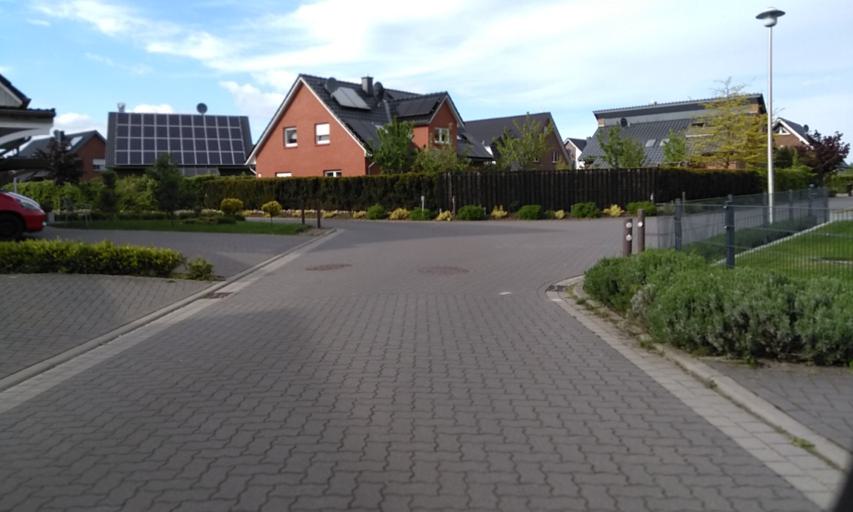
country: DE
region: Lower Saxony
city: Apensen
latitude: 53.4431
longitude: 9.6272
